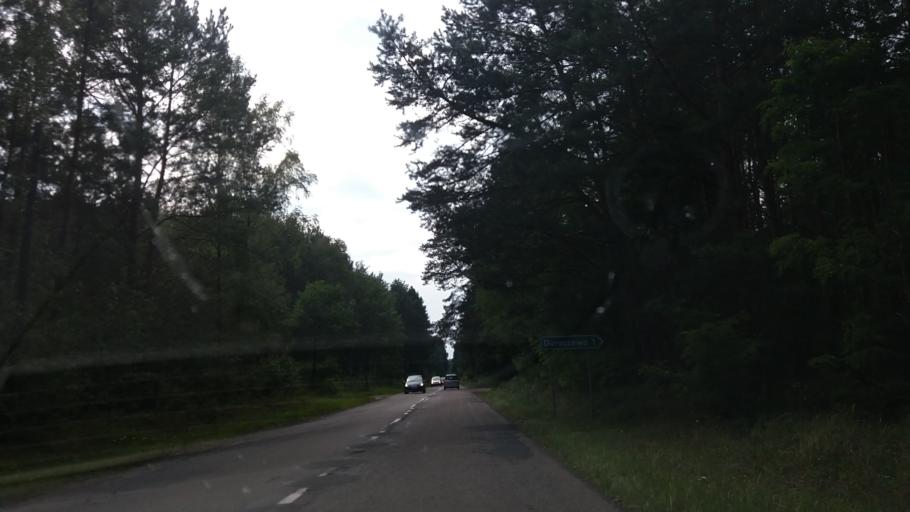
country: PL
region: Lubusz
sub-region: Powiat strzelecko-drezdenecki
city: Zwierzyn
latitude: 52.7349
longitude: 15.6329
